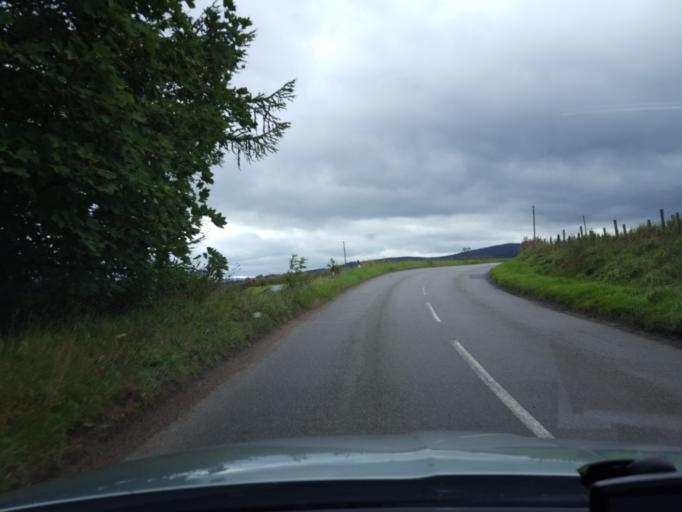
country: GB
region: Scotland
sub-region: Aberdeenshire
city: Kemnay
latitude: 57.1552
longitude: -2.4302
